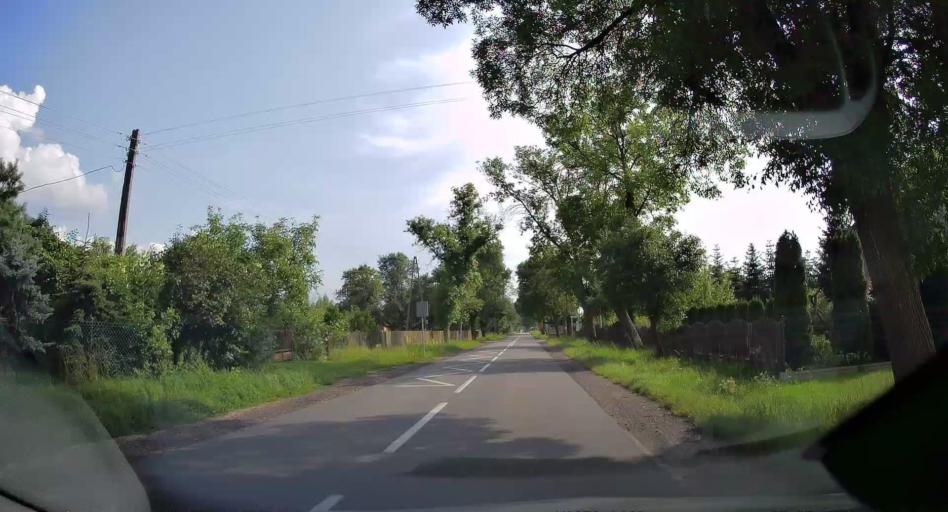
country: PL
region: Lodz Voivodeship
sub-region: Powiat tomaszowski
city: Rzeczyca
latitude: 51.5871
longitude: 20.2876
